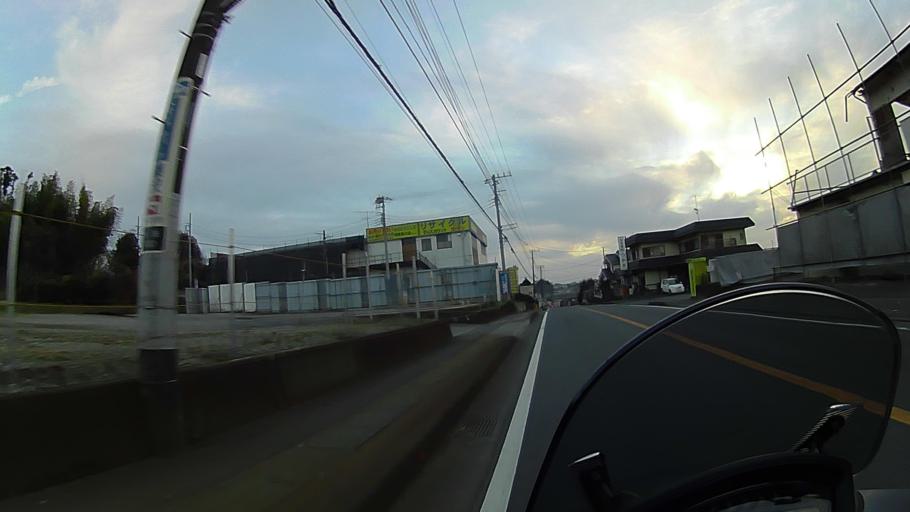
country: JP
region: Kanagawa
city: Atsugi
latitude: 35.4120
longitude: 139.4165
